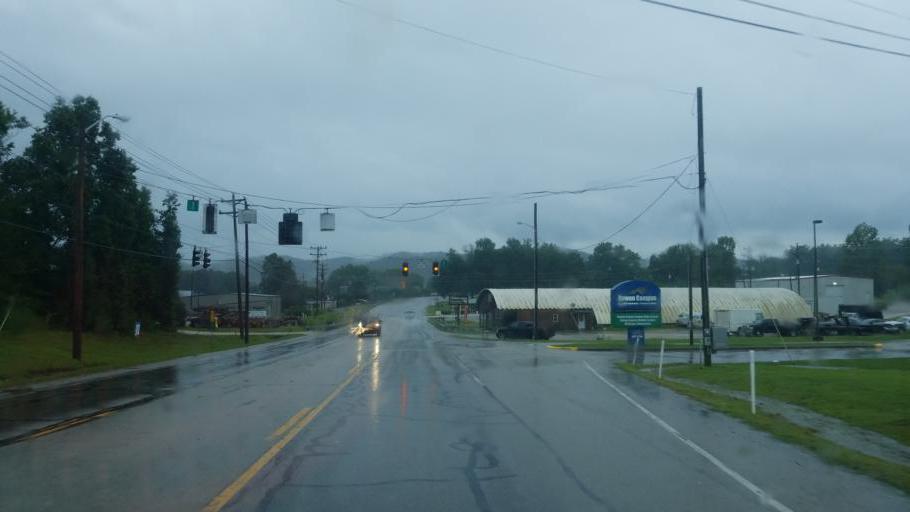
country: US
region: Kentucky
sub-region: Rowan County
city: Morehead
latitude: 38.2091
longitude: -83.4761
